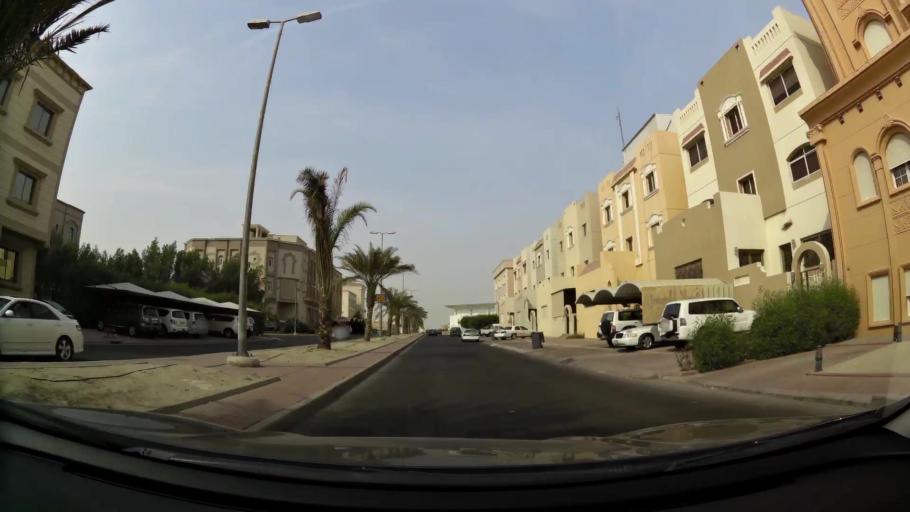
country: KW
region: Al Asimah
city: Ar Rabiyah
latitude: 29.2717
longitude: 47.9349
